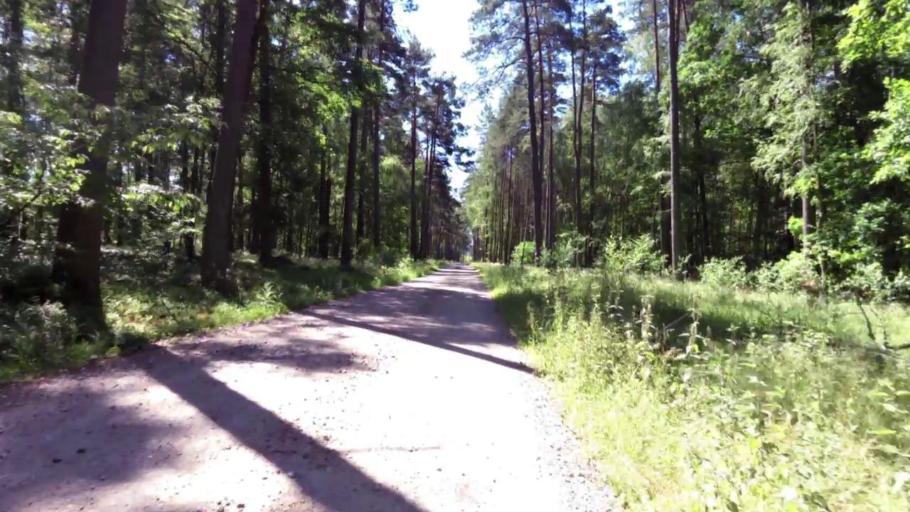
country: PL
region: West Pomeranian Voivodeship
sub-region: Powiat swidwinski
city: Rabino
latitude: 53.9074
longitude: 16.0069
